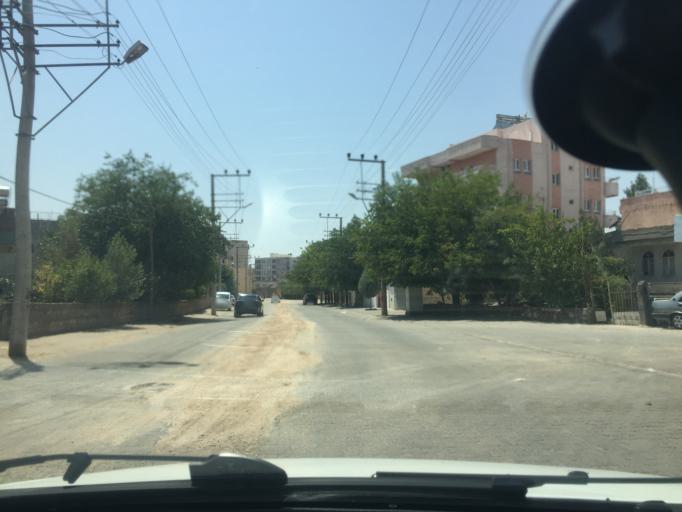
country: TR
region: Mardin
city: Midyat
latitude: 37.4291
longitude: 41.3427
